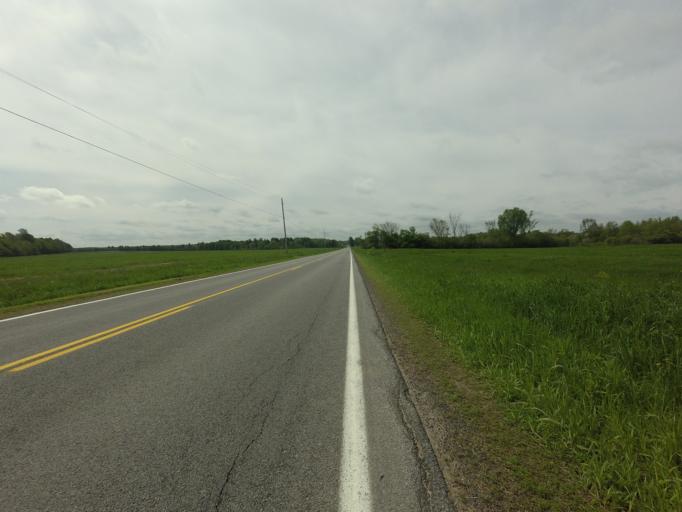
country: CA
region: Ontario
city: Cornwall
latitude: 44.7123
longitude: -74.6610
